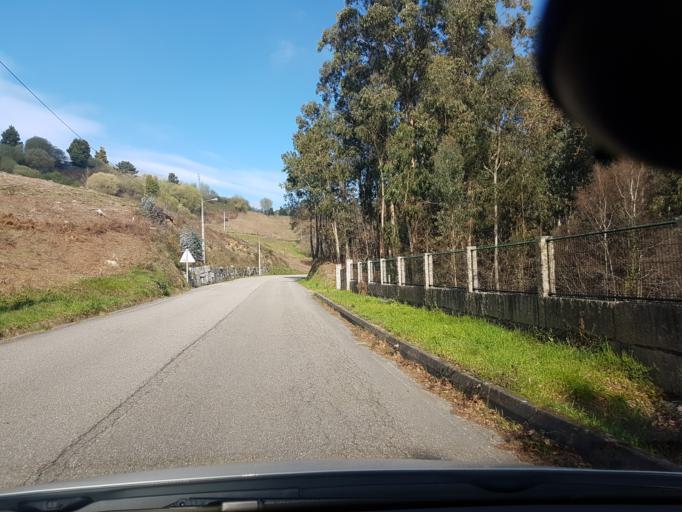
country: ES
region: Galicia
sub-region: Provincia de Pontevedra
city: Porrino
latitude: 42.2105
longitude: -8.6432
